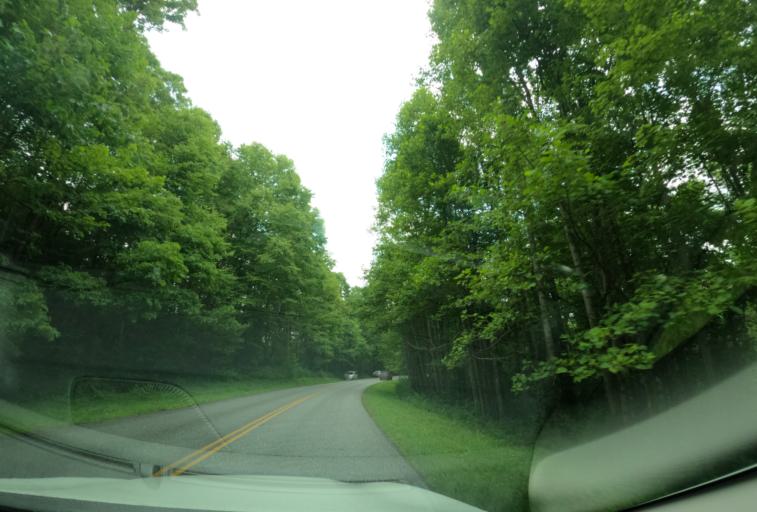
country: US
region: North Carolina
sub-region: Buncombe County
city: Avery Creek
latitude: 35.4815
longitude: -82.6018
